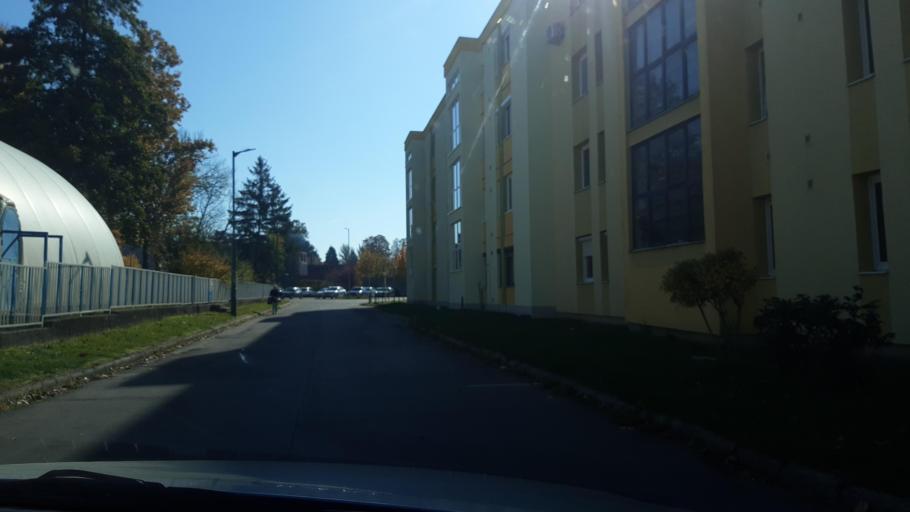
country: HU
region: Veszprem
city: Ajka
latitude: 47.1083
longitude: 17.5529
